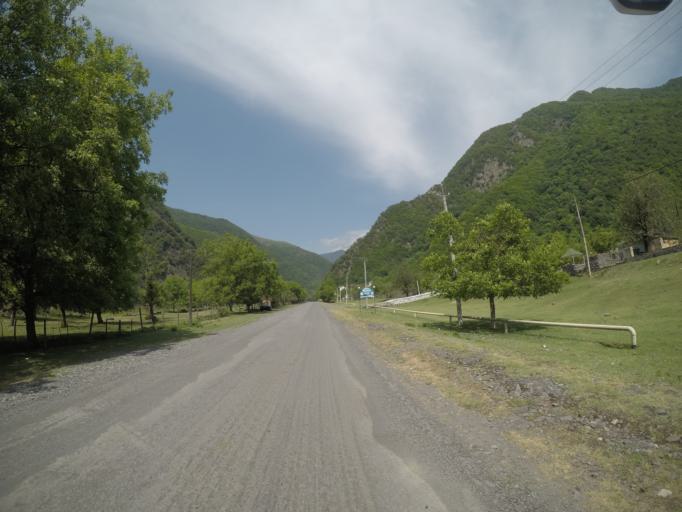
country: AZ
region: Qakh Rayon
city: Qaxbas
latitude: 41.4595
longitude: 47.0273
